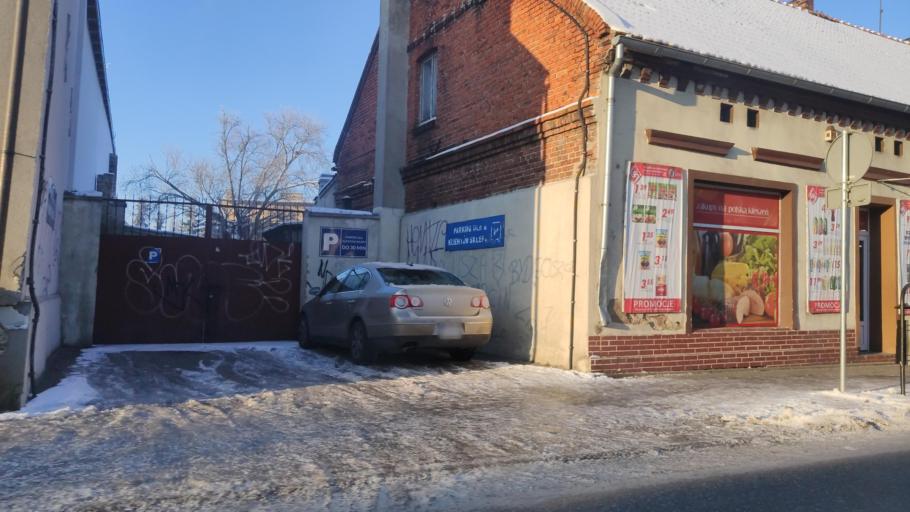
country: PL
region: Kujawsko-Pomorskie
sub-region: Powiat zninski
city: Barcin
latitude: 52.8633
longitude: 17.9465
